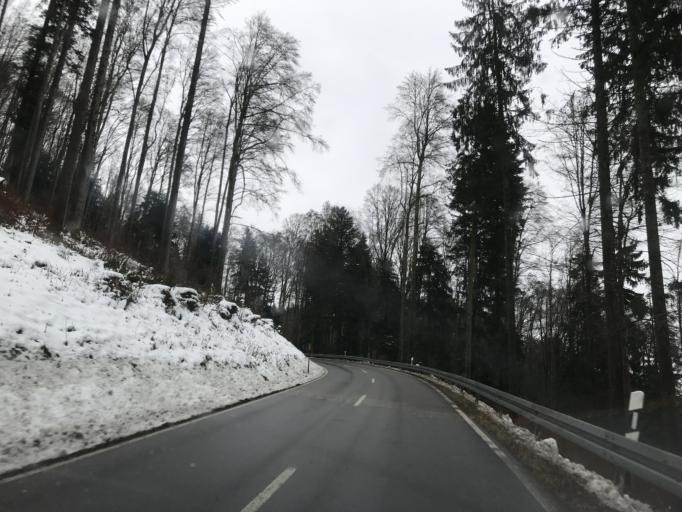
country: DE
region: Baden-Wuerttemberg
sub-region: Freiburg Region
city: Hasel
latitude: 47.6935
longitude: 7.8932
